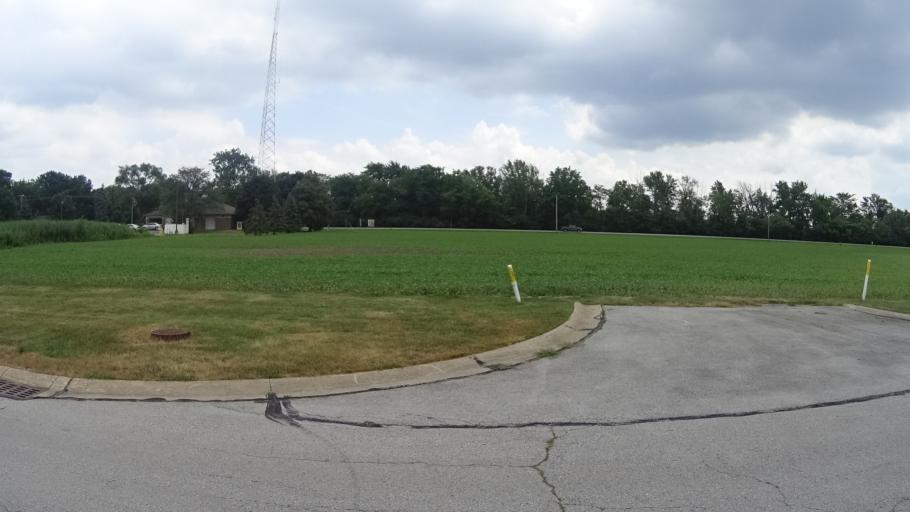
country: US
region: Ohio
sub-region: Erie County
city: Sandusky
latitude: 41.4441
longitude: -82.7749
